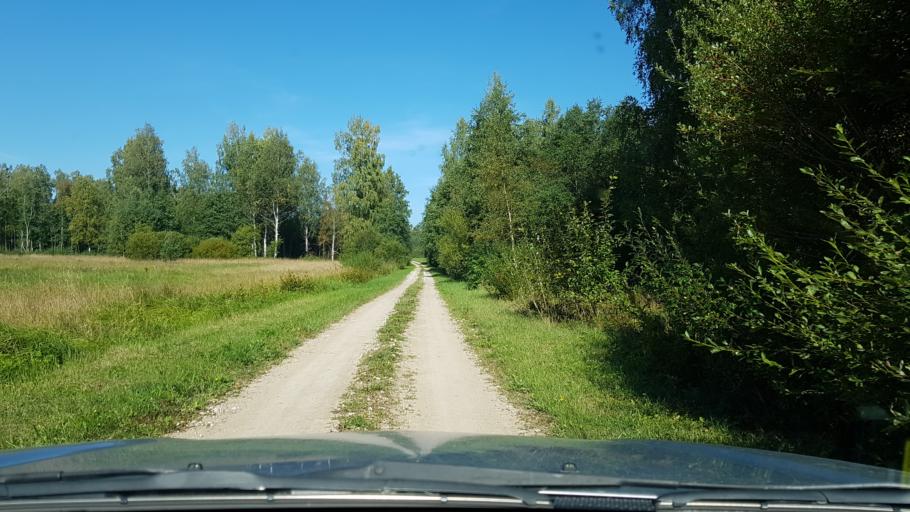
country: EE
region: Ida-Virumaa
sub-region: Sillamaee linn
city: Sillamae
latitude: 59.3285
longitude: 27.7749
